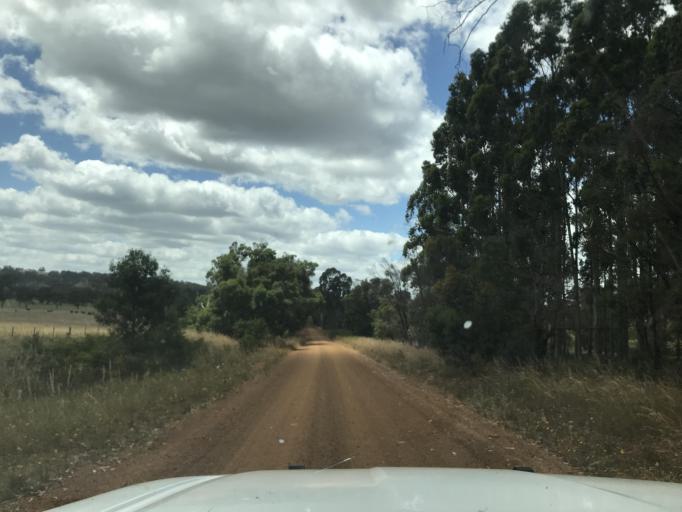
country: AU
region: South Australia
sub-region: Wattle Range
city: Penola
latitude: -37.3713
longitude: 141.2279
